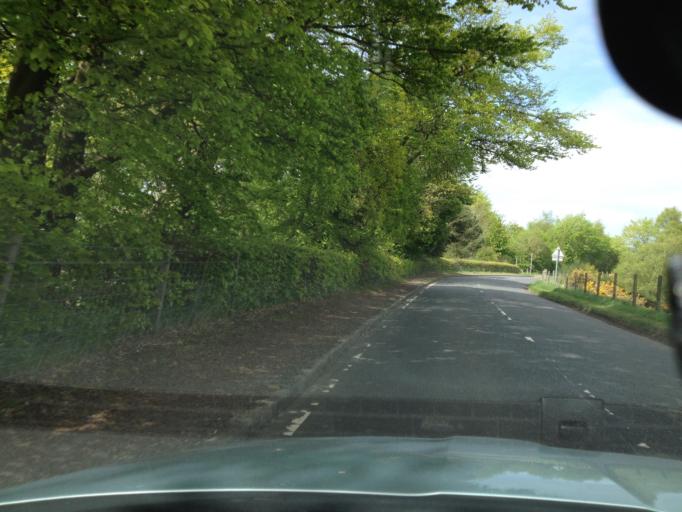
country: GB
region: Scotland
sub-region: West Lothian
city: West Calder
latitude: 55.8615
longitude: -3.5705
